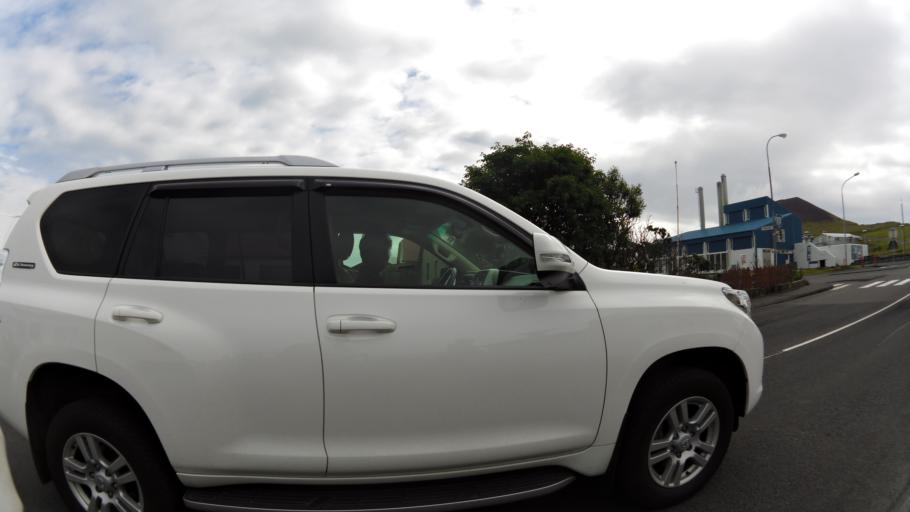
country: IS
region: South
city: Vestmannaeyjar
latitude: 63.4366
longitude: -20.2767
